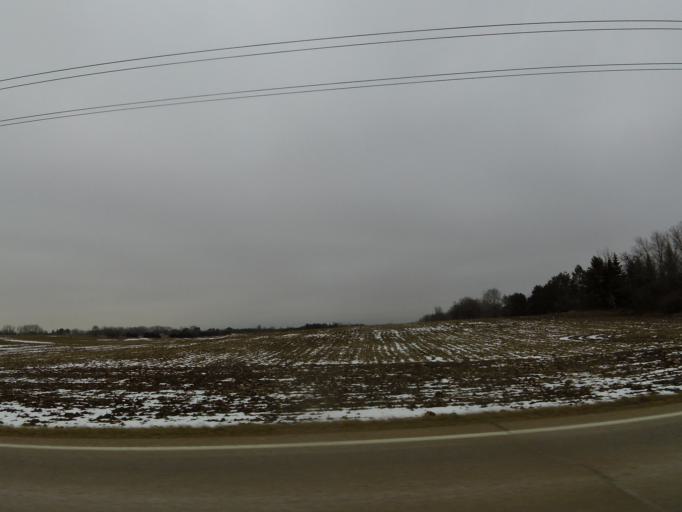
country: US
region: Minnesota
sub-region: Carver County
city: Carver
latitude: 44.7181
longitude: -93.6544
